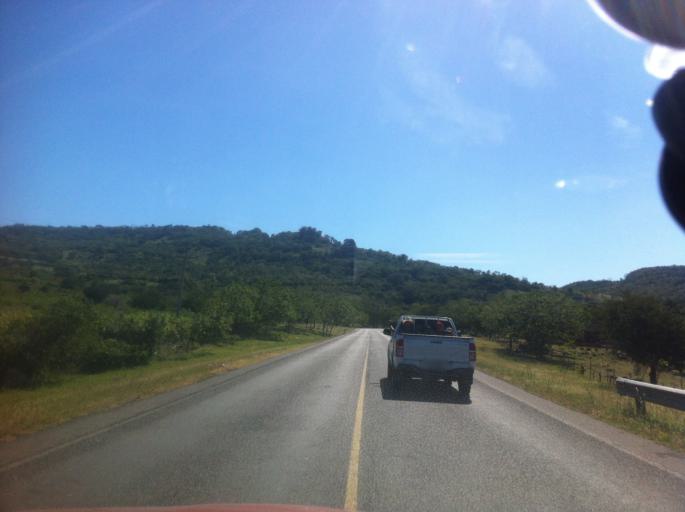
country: NI
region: Boaco
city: Teustepe
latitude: 12.3587
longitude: -85.8791
